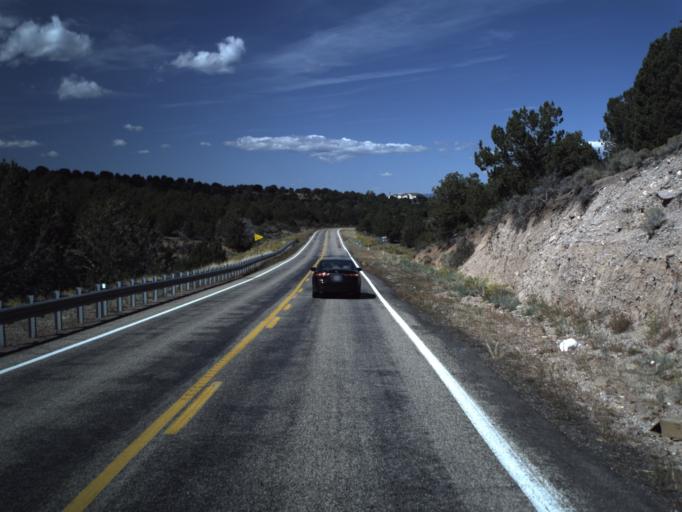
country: US
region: Utah
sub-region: Washington County
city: Enterprise
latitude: 37.5544
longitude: -113.6886
